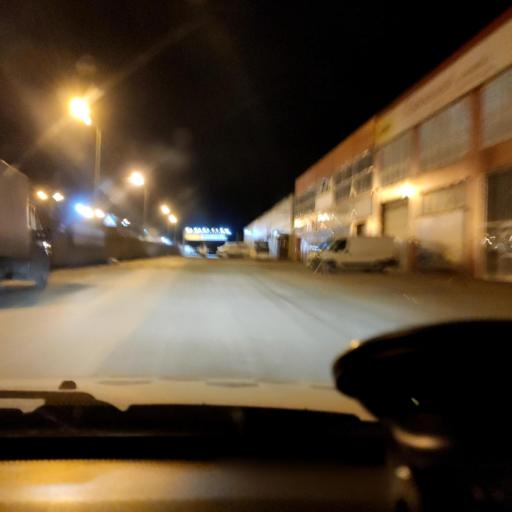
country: RU
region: Perm
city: Froly
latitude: 57.9582
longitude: 56.2762
